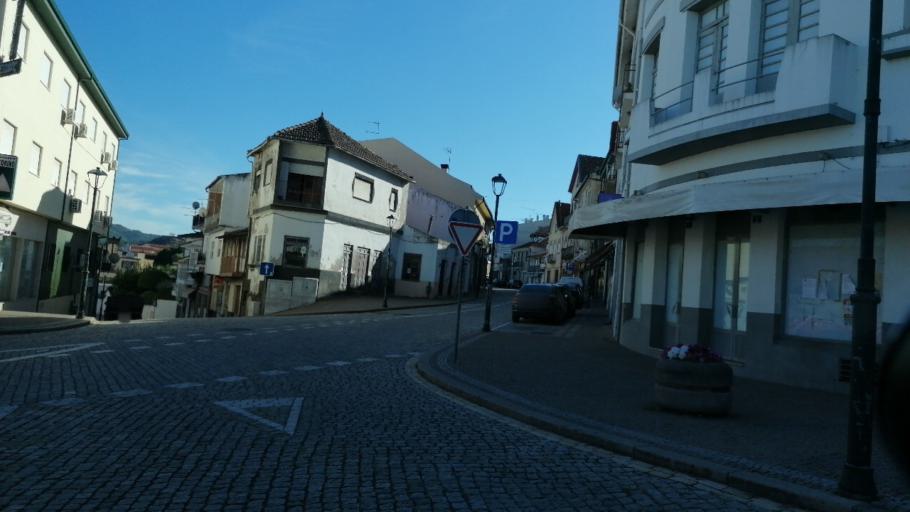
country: PT
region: Vila Real
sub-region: Murca
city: Murca
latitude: 41.4072
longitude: -7.4536
